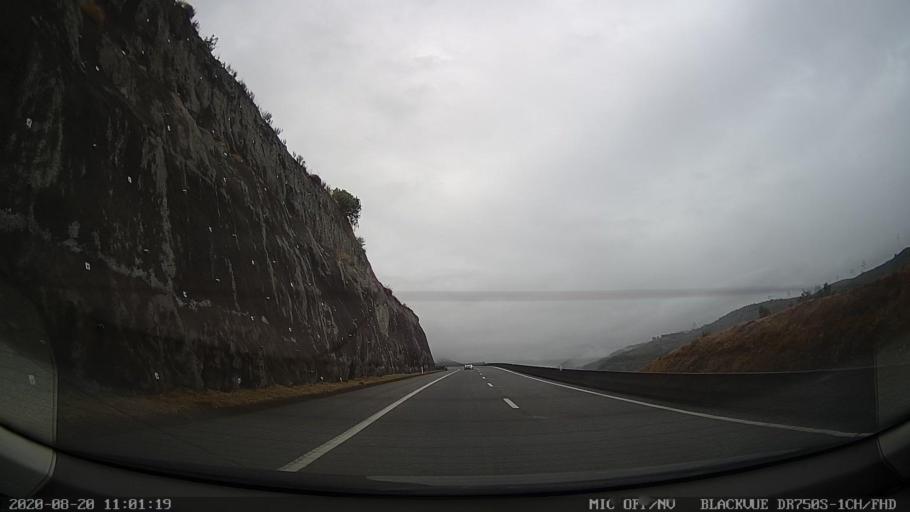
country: PT
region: Vila Real
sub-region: Peso da Regua
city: Peso da Regua
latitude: 41.1837
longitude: -7.7524
